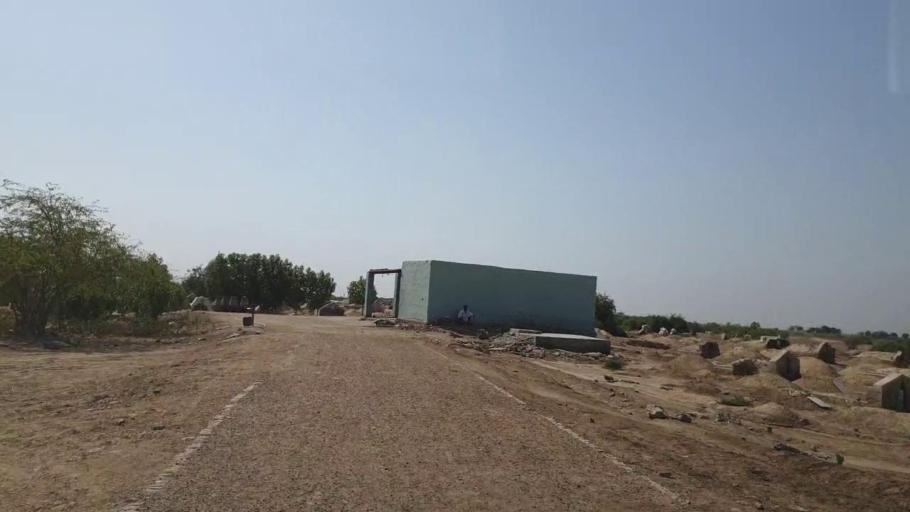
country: PK
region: Sindh
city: Naukot
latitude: 24.9706
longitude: 69.4695
